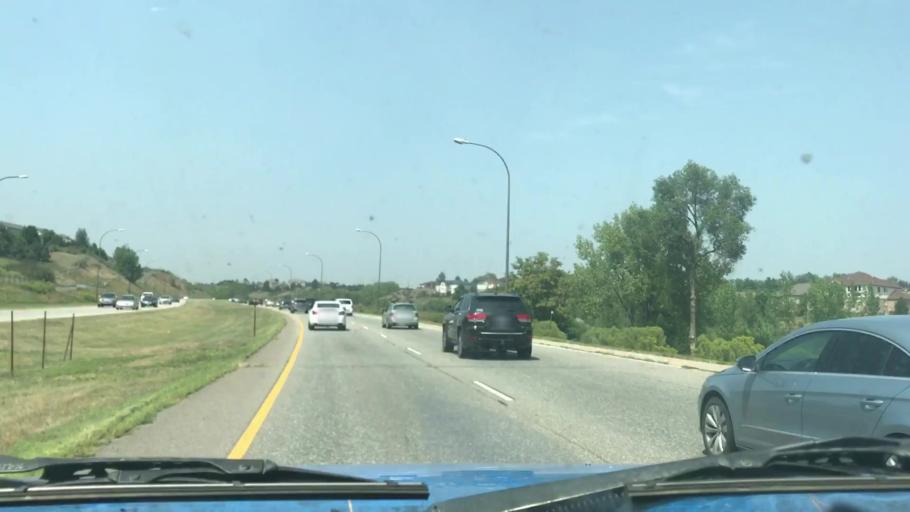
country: US
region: Colorado
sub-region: Jefferson County
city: Lakewood
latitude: 39.6695
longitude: -105.1148
